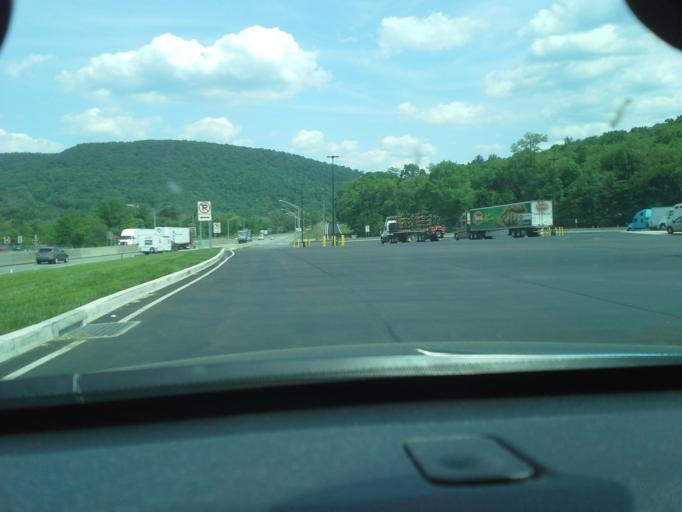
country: US
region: Pennsylvania
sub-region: Bedford County
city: Bedford
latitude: 40.0302
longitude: -78.4925
